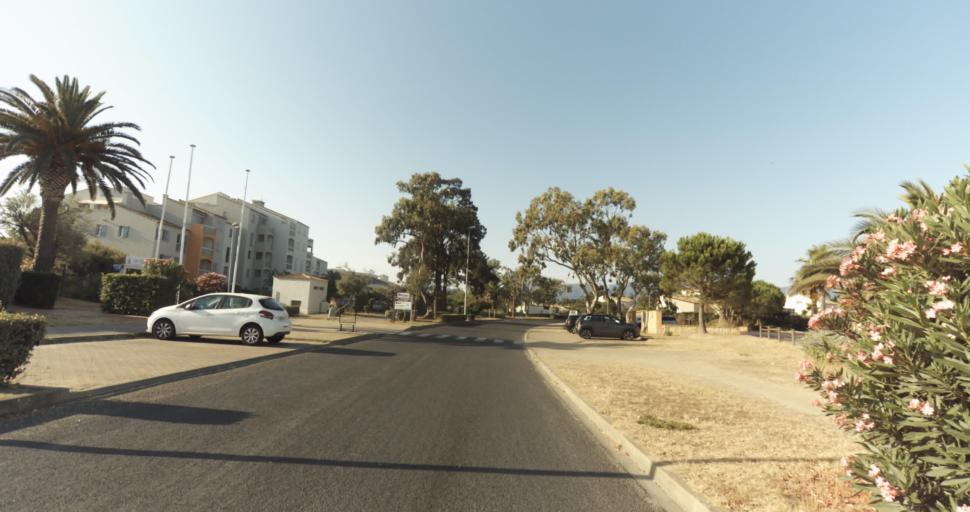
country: FR
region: Languedoc-Roussillon
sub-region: Departement des Pyrenees-Orientales
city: Saint-Cyprien-Plage
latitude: 42.6029
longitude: 3.0400
